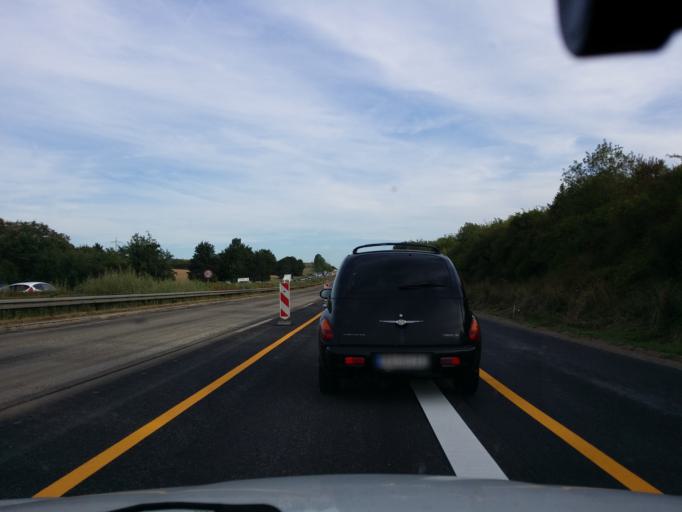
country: DE
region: Hesse
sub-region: Regierungsbezirk Giessen
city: Villmar
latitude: 50.3506
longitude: 8.1645
